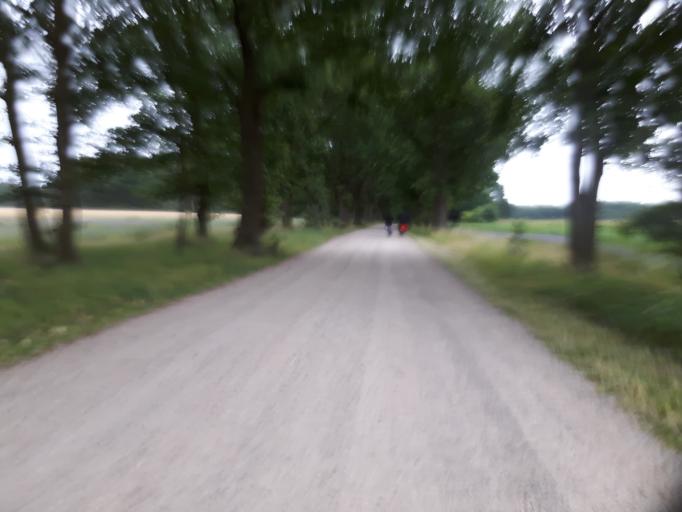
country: DE
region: Lower Saxony
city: Winsen
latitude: 53.3219
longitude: 10.1980
